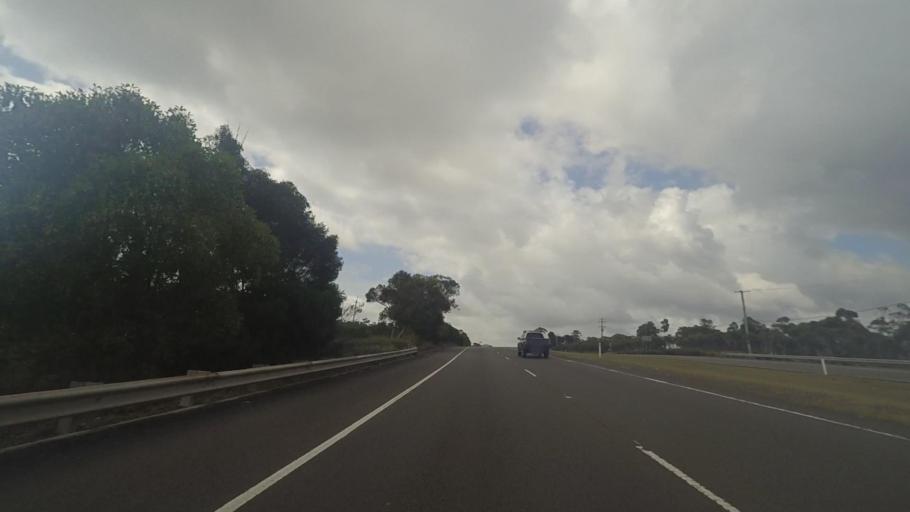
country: AU
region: New South Wales
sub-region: Sutherland Shire
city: Heathcote
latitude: -34.1052
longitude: 150.9939
